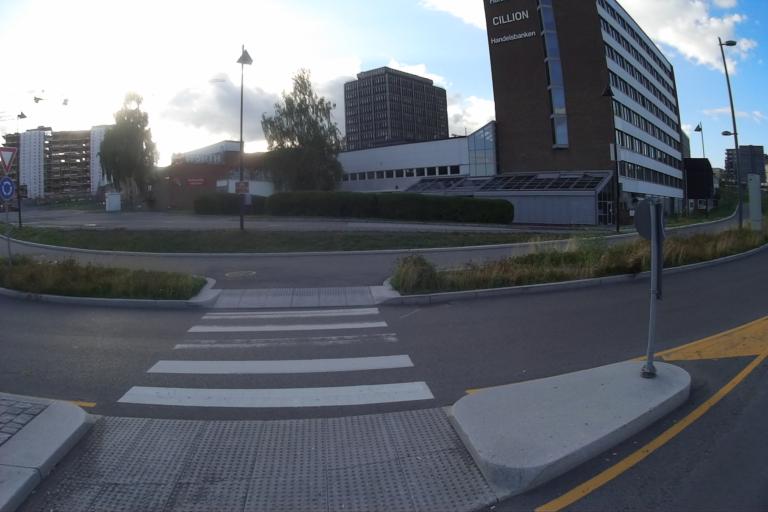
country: NO
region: Oslo
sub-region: Oslo
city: Oslo
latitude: 59.9292
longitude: 10.8015
